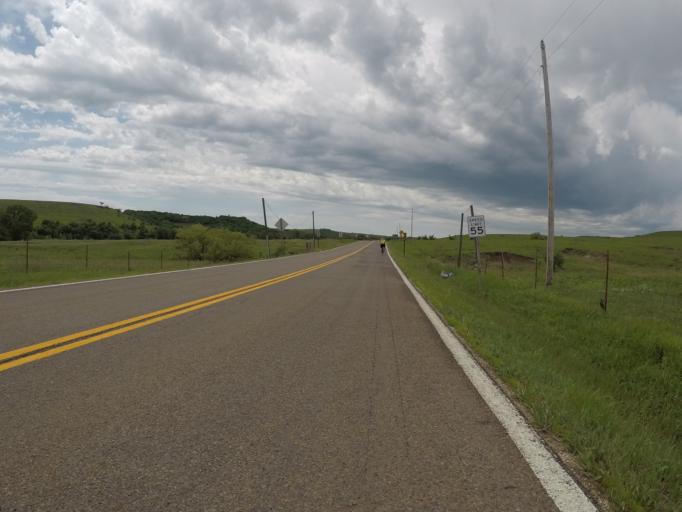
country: US
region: Kansas
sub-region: Wabaunsee County
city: Alma
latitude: 38.8901
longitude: -96.2810
